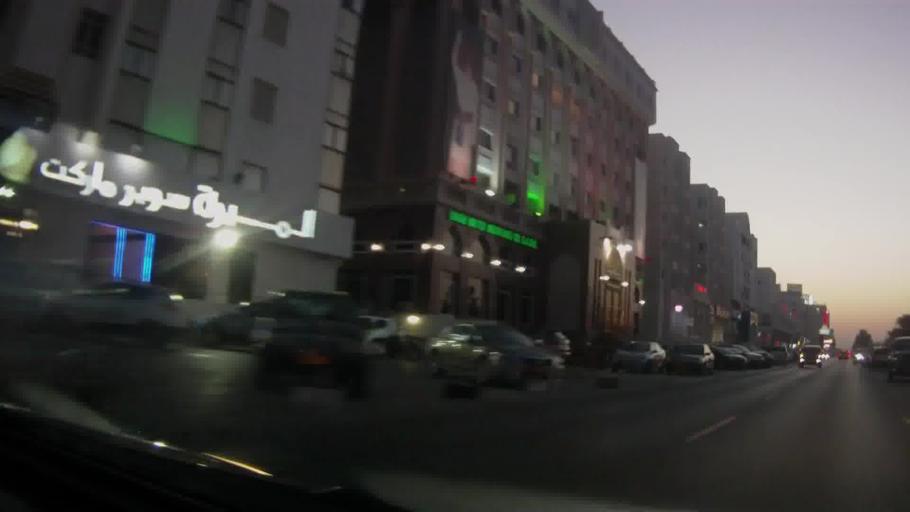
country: OM
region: Muhafazat Masqat
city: Bawshar
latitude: 23.5968
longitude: 58.4302
